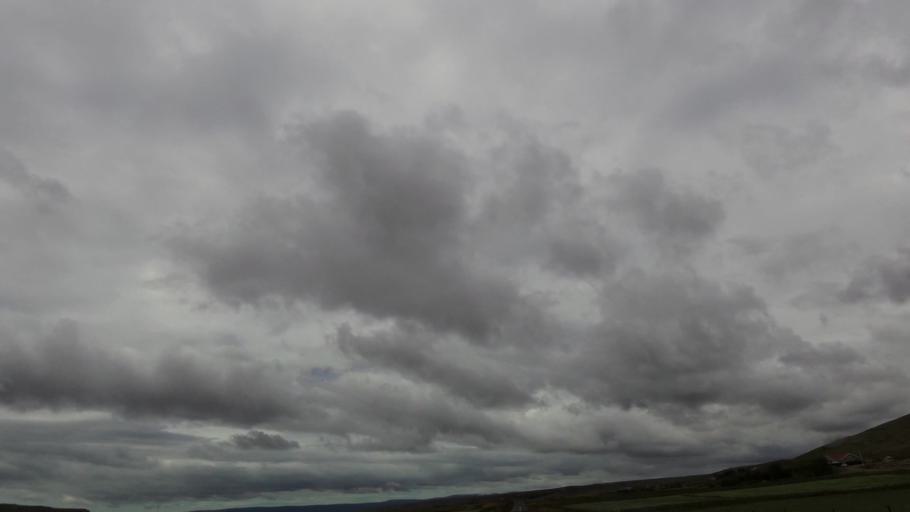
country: IS
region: West
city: Borgarnes
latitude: 64.9999
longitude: -21.6274
